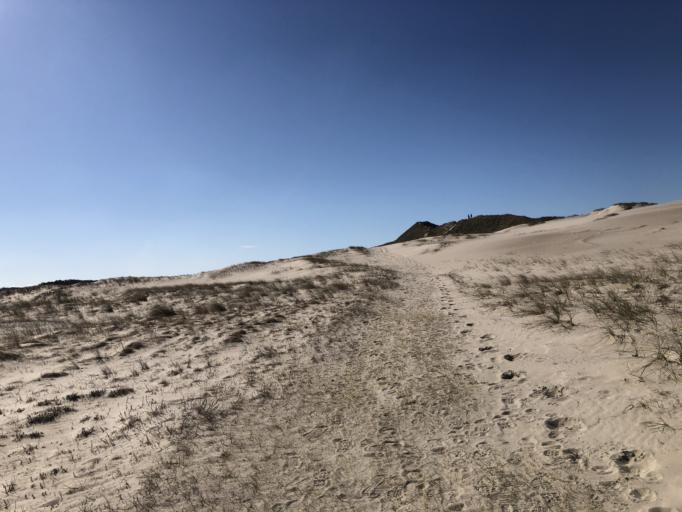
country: DK
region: Central Jutland
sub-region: Holstebro Kommune
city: Ulfborg
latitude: 56.3106
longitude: 8.1268
